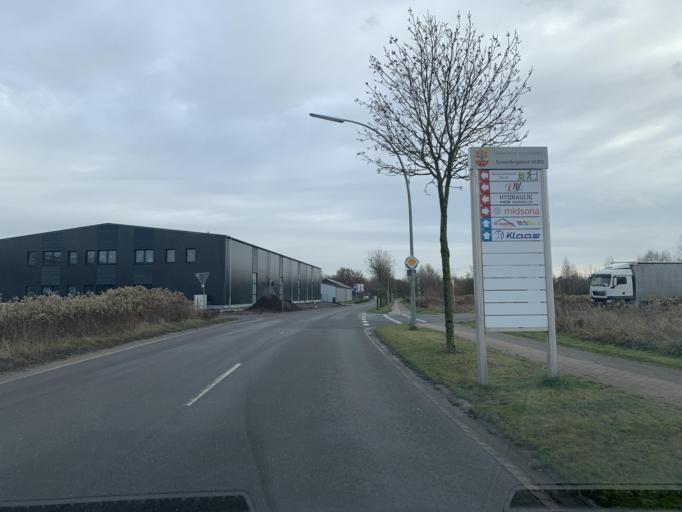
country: DE
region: North Rhine-Westphalia
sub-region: Regierungsbezirk Munster
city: Ascheberg
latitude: 51.7991
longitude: 7.6242
